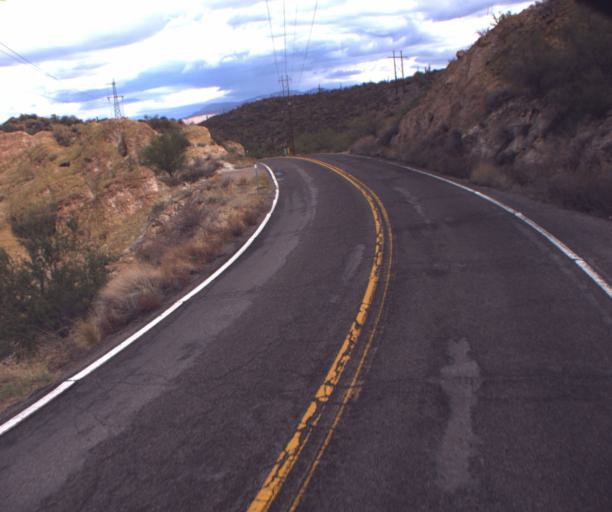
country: US
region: Arizona
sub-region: Pinal County
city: Apache Junction
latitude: 33.5269
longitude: -111.4538
